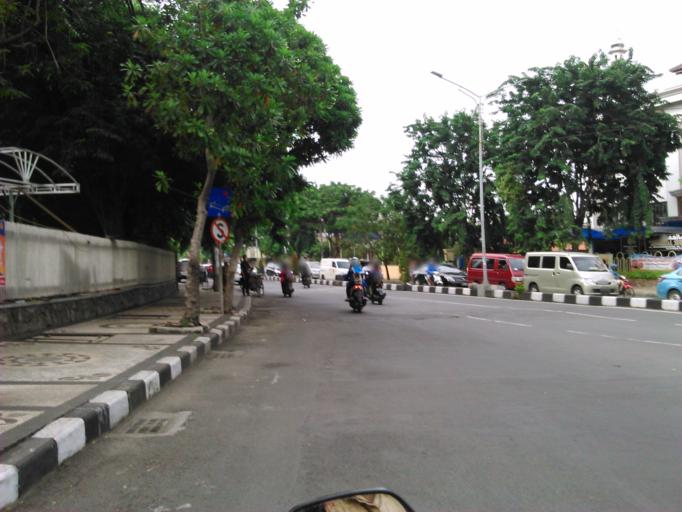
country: ID
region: East Java
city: Gubengairlangga
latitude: -7.2659
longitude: 112.7569
